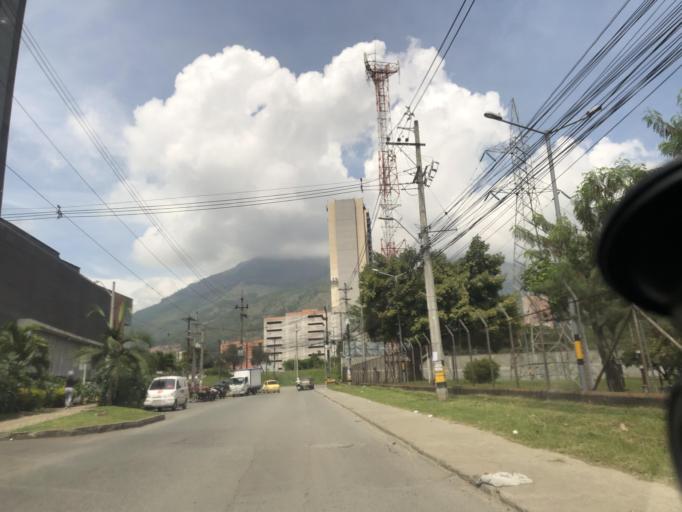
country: CO
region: Antioquia
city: Bello
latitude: 6.3384
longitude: -75.5387
